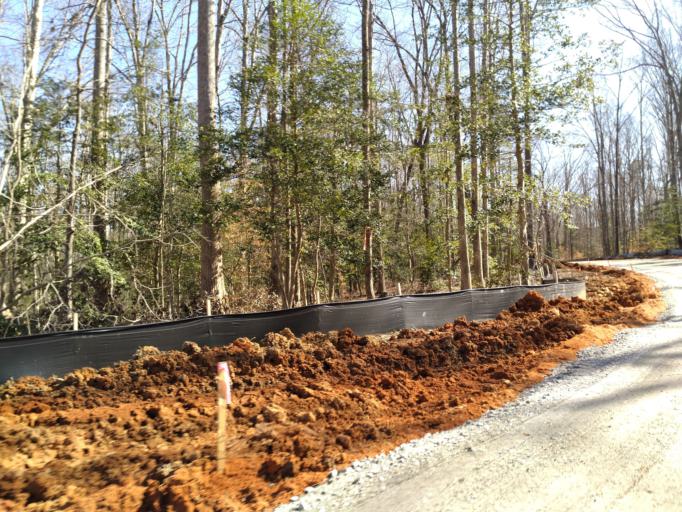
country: US
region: Virginia
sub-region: Chesterfield County
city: Chesterfield
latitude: 37.3799
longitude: -77.5582
